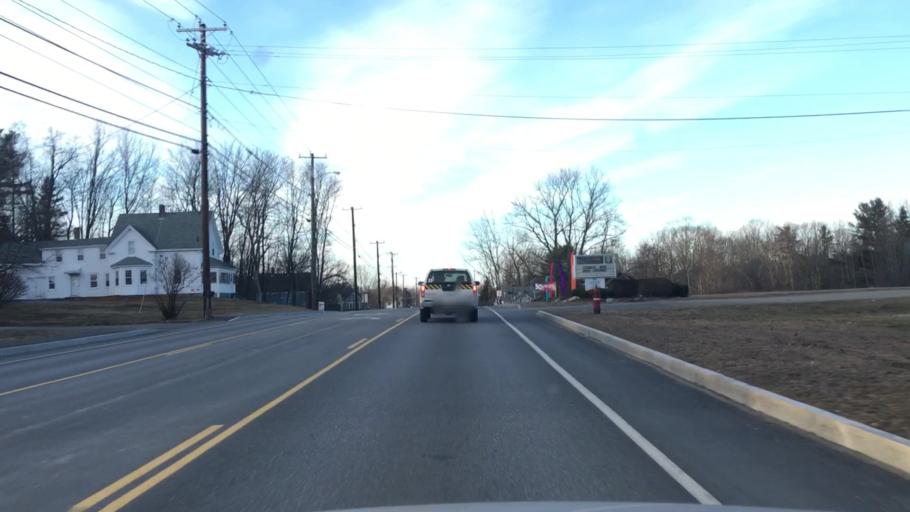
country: US
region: Maine
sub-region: Hancock County
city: Ellsworth
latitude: 44.5555
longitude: -68.4320
